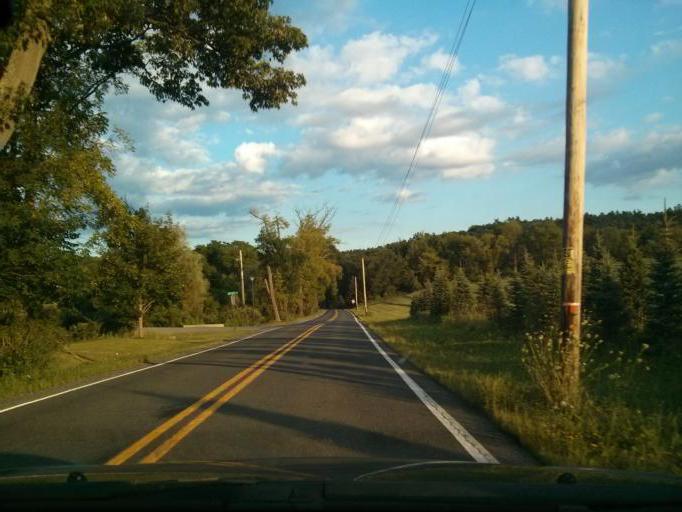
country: US
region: Pennsylvania
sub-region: Centre County
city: Park Forest Village
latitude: 40.8365
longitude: -77.9321
